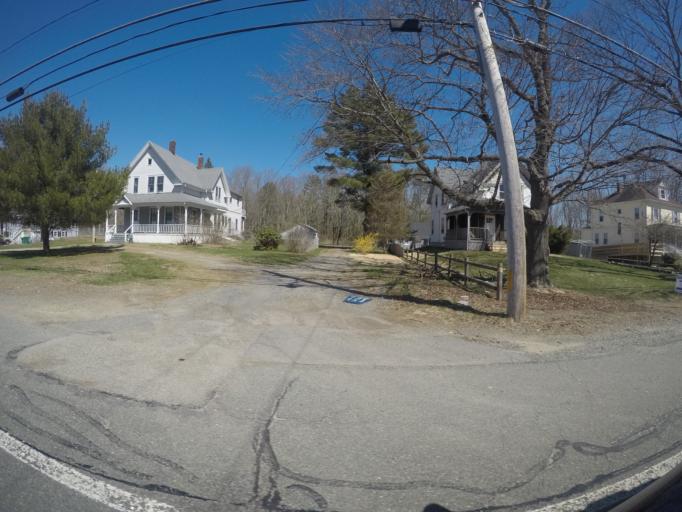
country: US
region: Massachusetts
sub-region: Norfolk County
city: Stoughton
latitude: 42.0717
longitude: -71.0875
